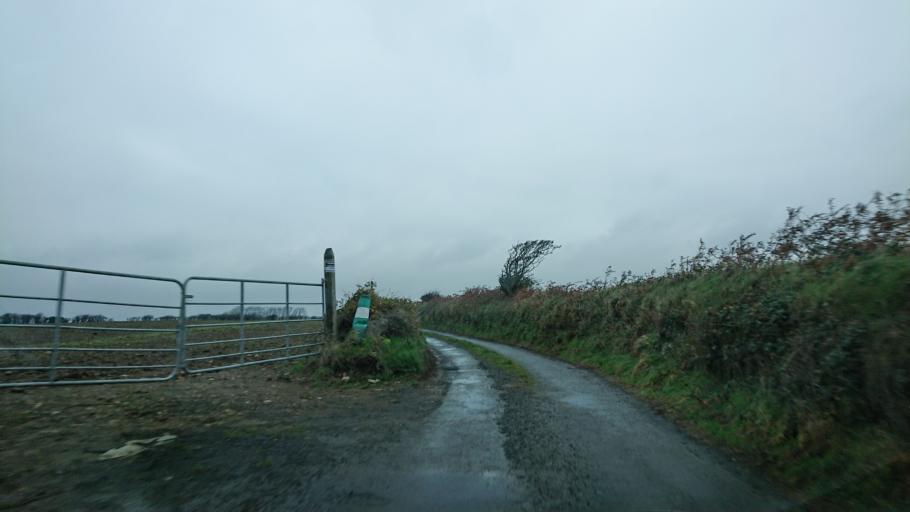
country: IE
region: Munster
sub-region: Waterford
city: Tra Mhor
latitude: 52.1966
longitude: -7.1367
